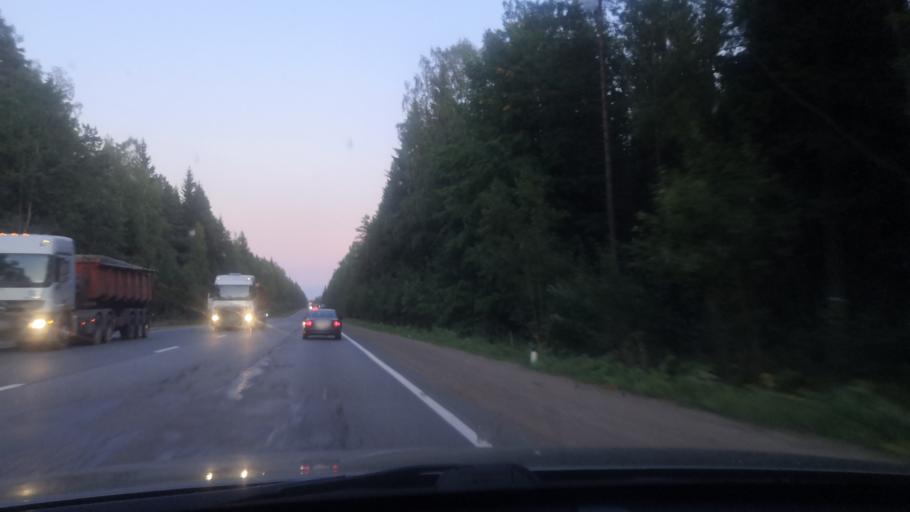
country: RU
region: St.-Petersburg
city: Pesochnyy
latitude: 60.1864
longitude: 30.1104
